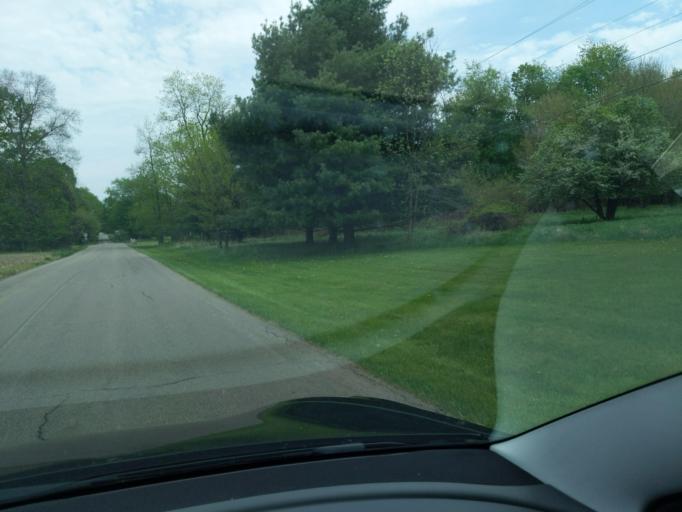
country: US
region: Michigan
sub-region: Ingham County
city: Mason
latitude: 42.5112
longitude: -84.5380
